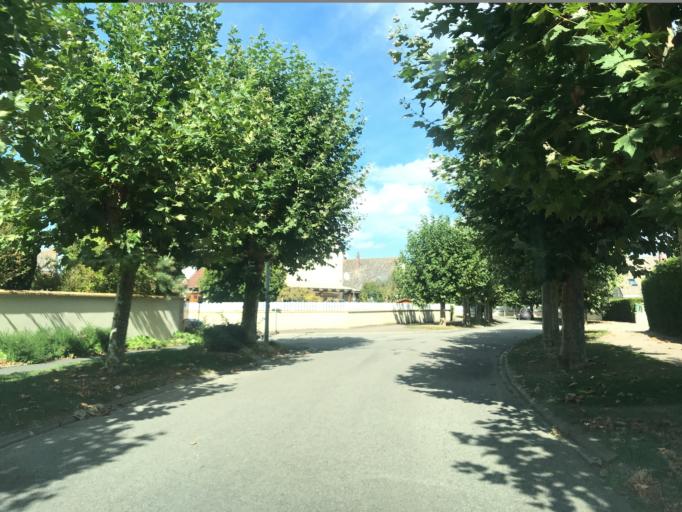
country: FR
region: Haute-Normandie
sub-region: Departement de l'Eure
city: Gaillon
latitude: 49.1613
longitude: 1.3440
